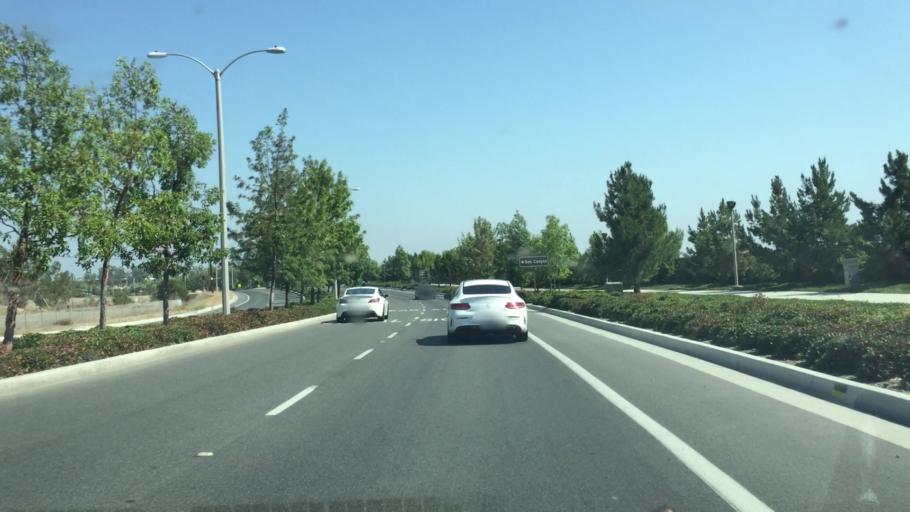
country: US
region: California
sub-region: Orange County
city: North Tustin
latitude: 33.7132
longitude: -117.7391
